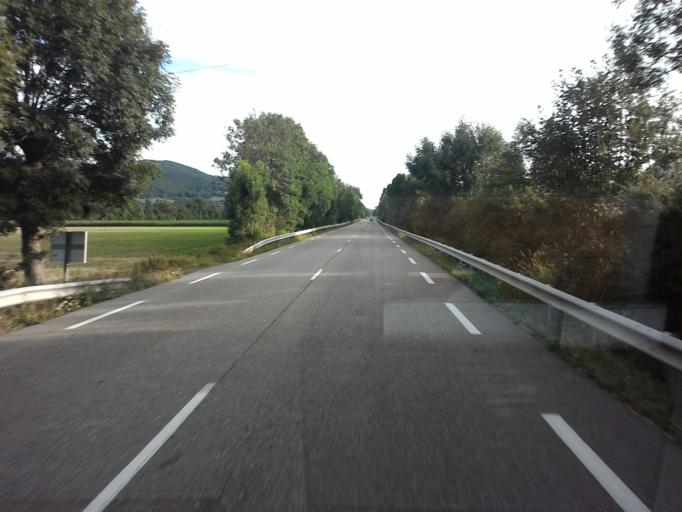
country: FR
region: Rhone-Alpes
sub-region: Departement de l'Isere
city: Pierre-Chatel
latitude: 44.9396
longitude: 5.7807
